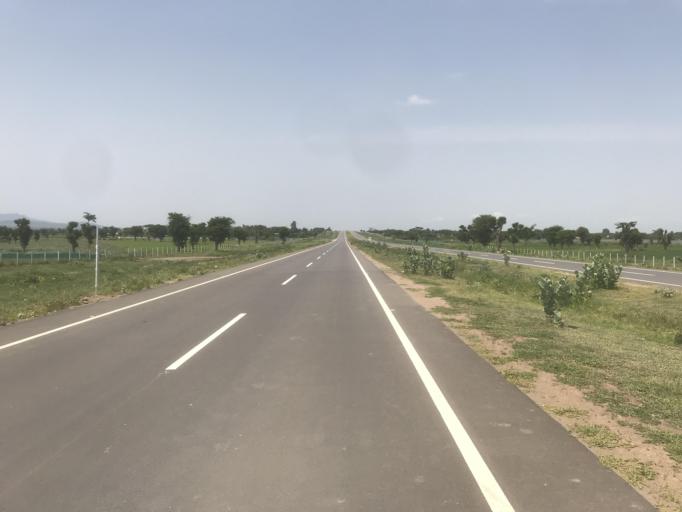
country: ET
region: Oromiya
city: Mojo
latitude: 8.3737
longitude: 38.9988
